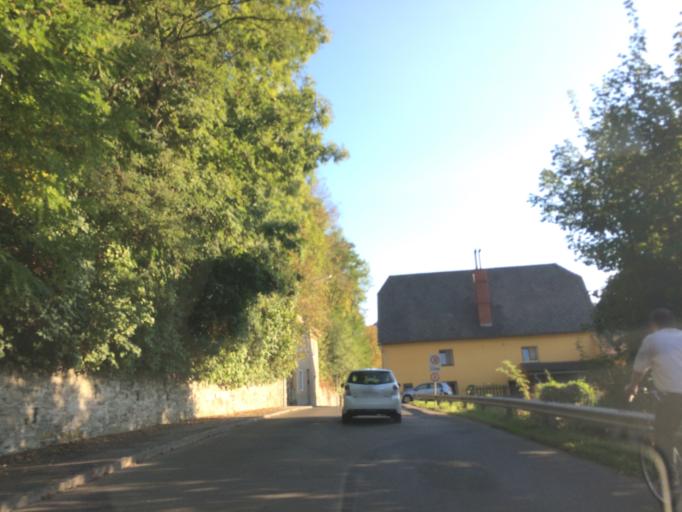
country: AT
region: Styria
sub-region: Politischer Bezirk Leoben
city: Leoben
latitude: 47.3690
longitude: 15.0980
